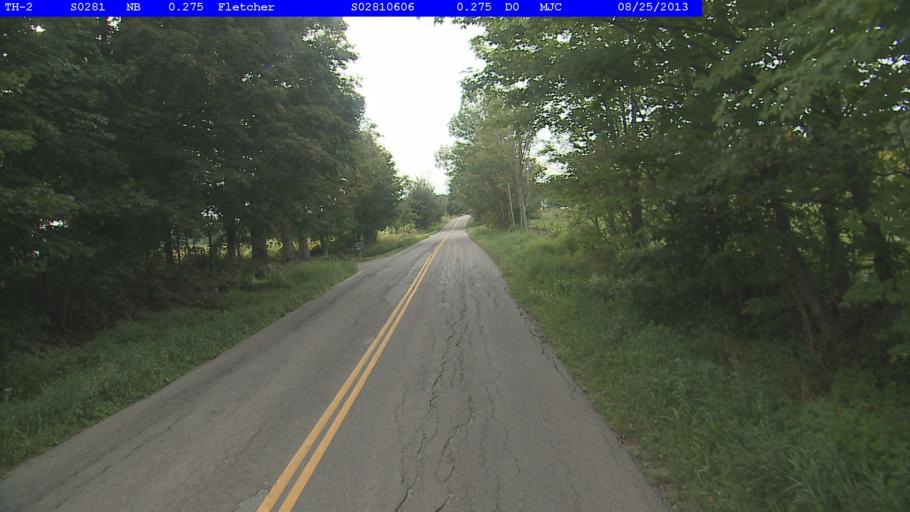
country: US
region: Vermont
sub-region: Chittenden County
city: Milton
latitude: 44.6851
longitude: -72.9193
